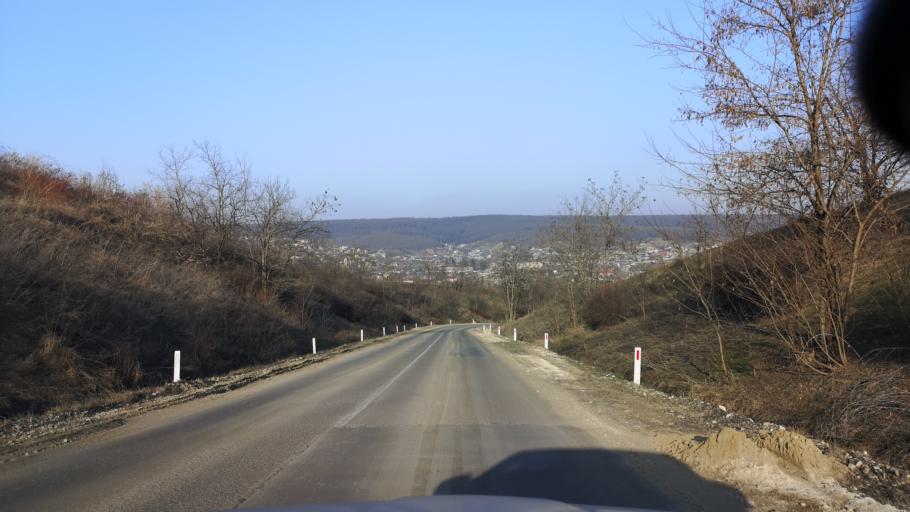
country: MD
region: Stinga Nistrului
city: Bucovat
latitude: 47.1073
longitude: 28.4987
